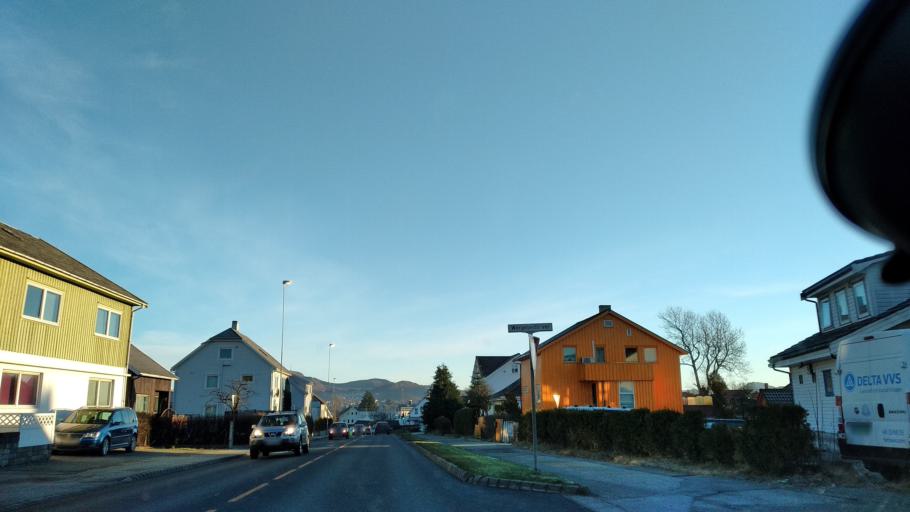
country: NO
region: Rogaland
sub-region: Sandnes
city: Sandnes
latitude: 58.8539
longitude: 5.7185
